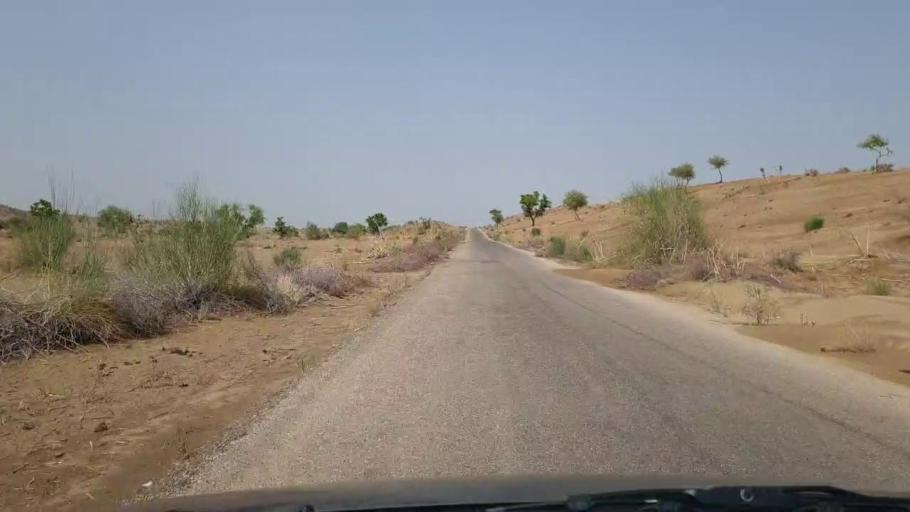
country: PK
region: Sindh
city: Chor
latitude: 25.4613
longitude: 70.4831
